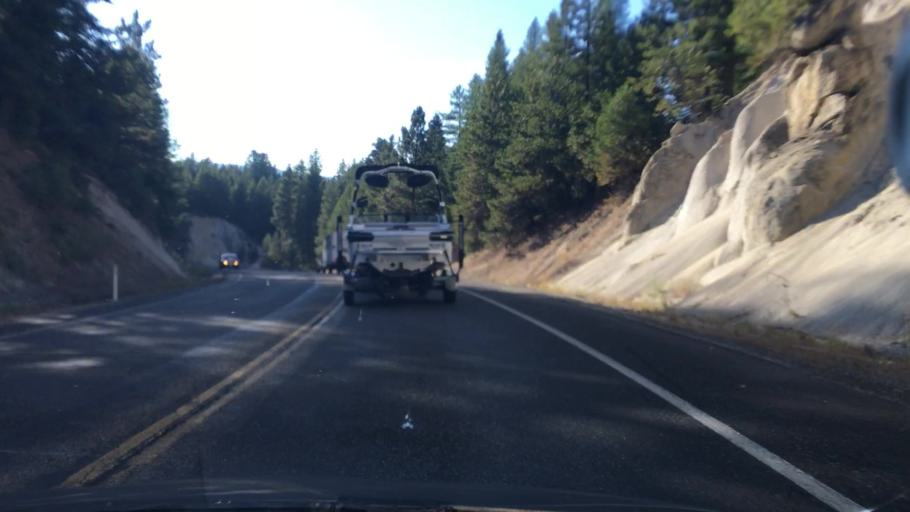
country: US
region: Idaho
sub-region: Valley County
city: Cascade
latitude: 44.5789
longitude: -116.0361
